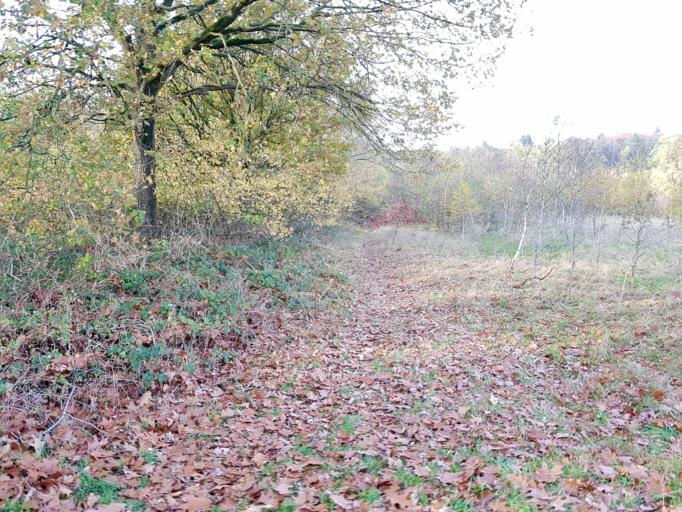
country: NL
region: North Brabant
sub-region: Gemeente Cuijk
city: Cuijk
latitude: 51.7553
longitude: 5.8959
